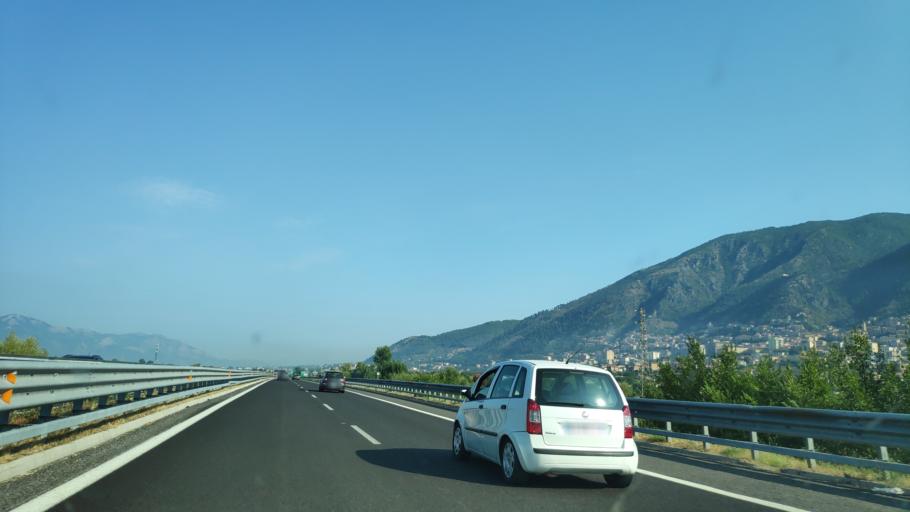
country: IT
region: Campania
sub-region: Provincia di Salerno
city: Sala Consilina
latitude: 40.3836
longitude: 15.5923
